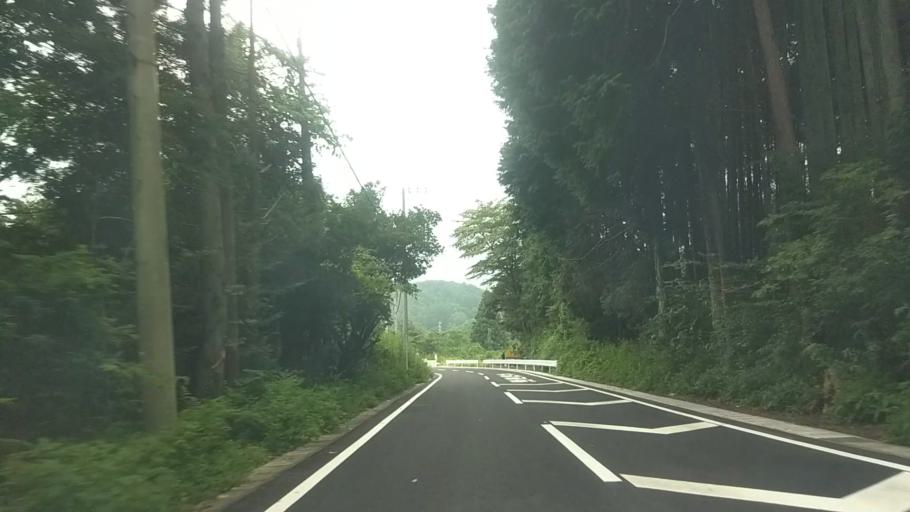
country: JP
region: Chiba
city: Kisarazu
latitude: 35.2643
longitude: 140.0490
